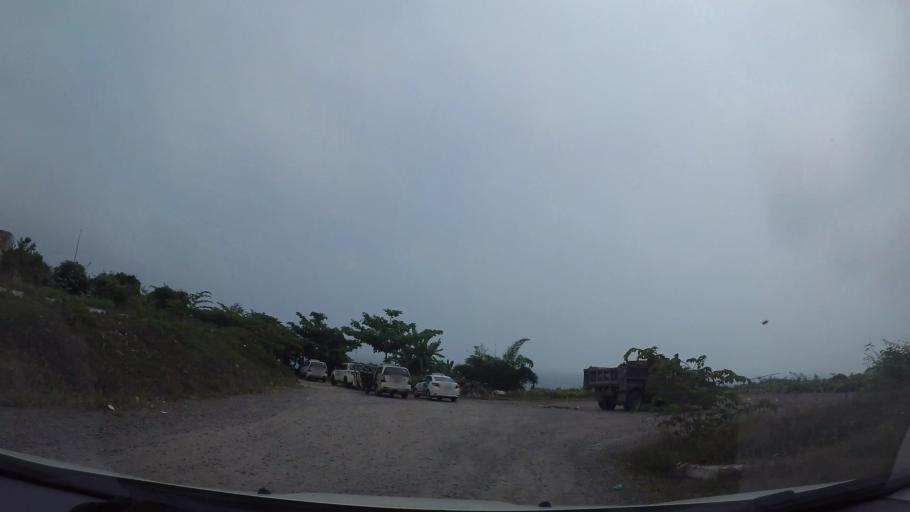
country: VN
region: Da Nang
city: Son Tra
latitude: 16.1135
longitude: 108.3099
